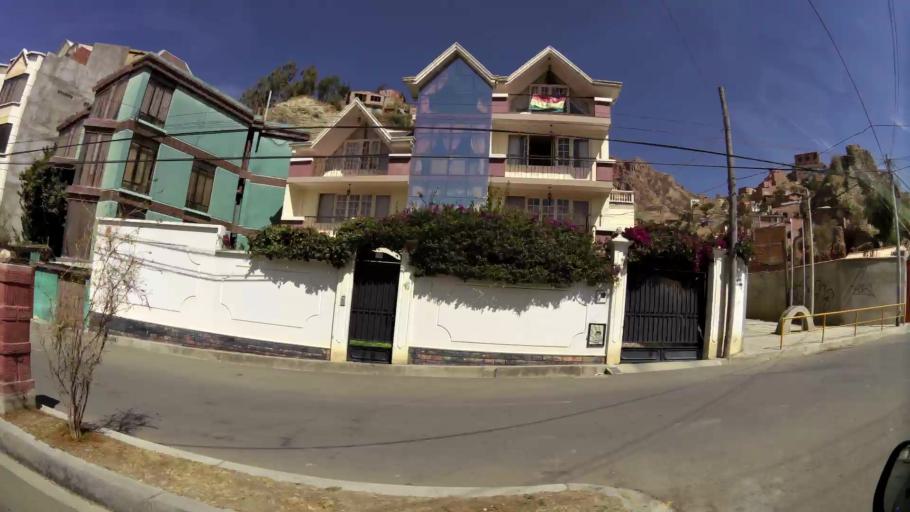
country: BO
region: La Paz
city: La Paz
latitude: -16.5439
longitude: -68.0967
